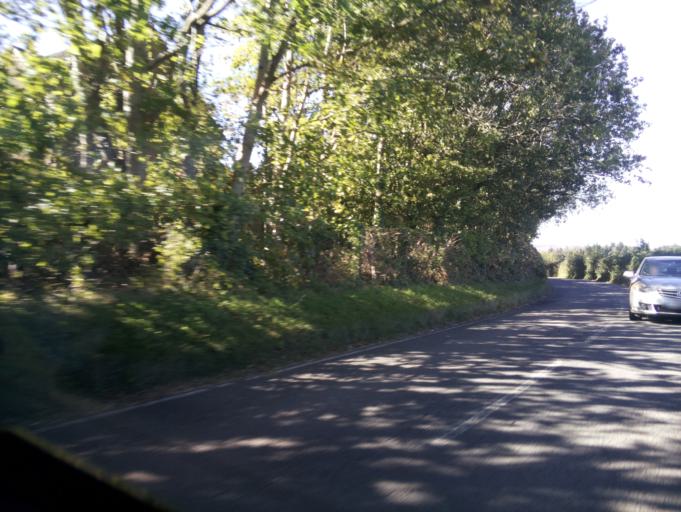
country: GB
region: Wales
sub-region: Newport
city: Newport
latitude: 51.5963
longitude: -3.0450
